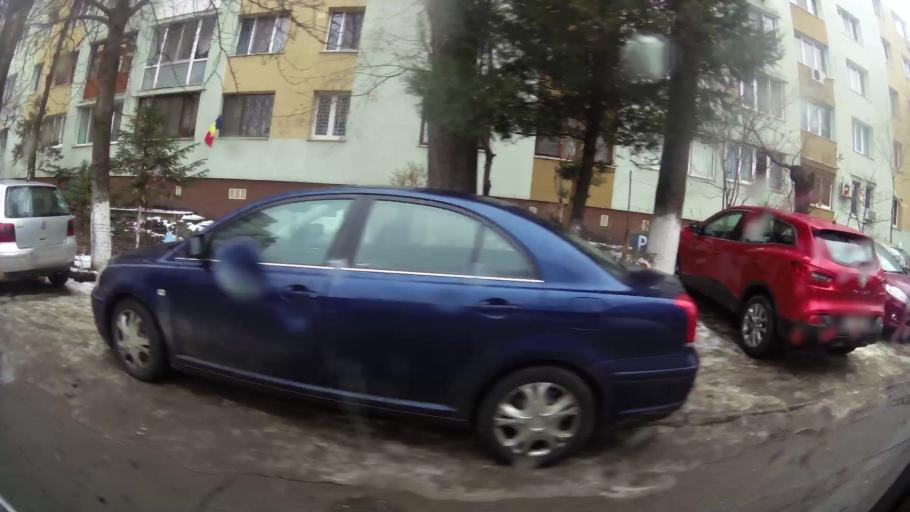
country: RO
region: Ilfov
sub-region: Comuna Chiajna
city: Rosu
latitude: 44.4233
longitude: 26.0213
